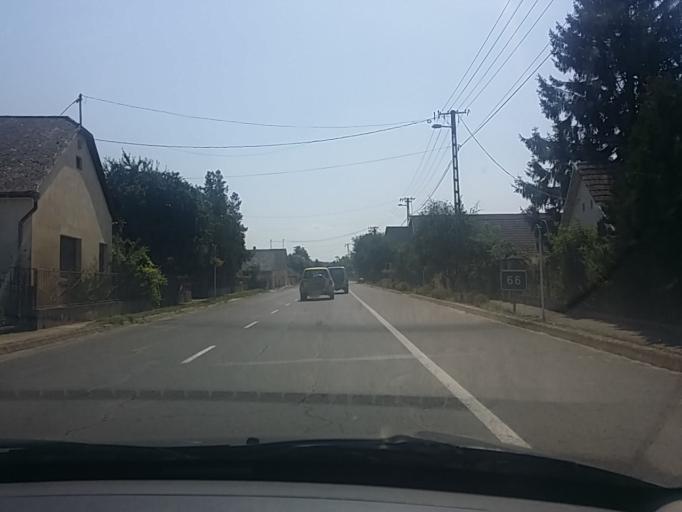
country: HU
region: Tolna
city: Tamasi
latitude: 46.5884
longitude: 18.2050
